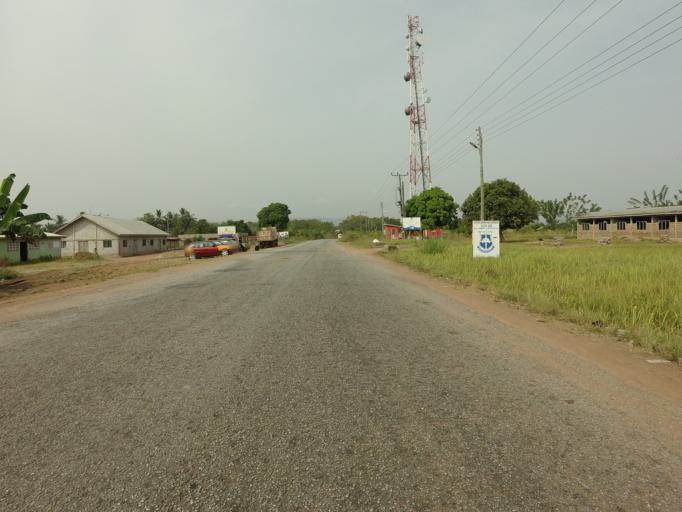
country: GH
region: Volta
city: Ho
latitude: 6.5727
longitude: 0.3645
